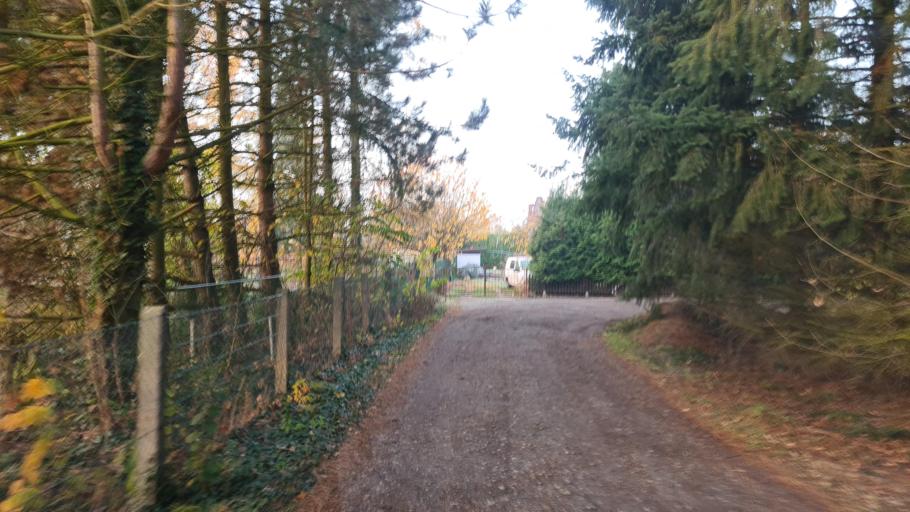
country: DE
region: Saxony-Anhalt
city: Jessen
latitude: 51.7975
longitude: 13.0069
